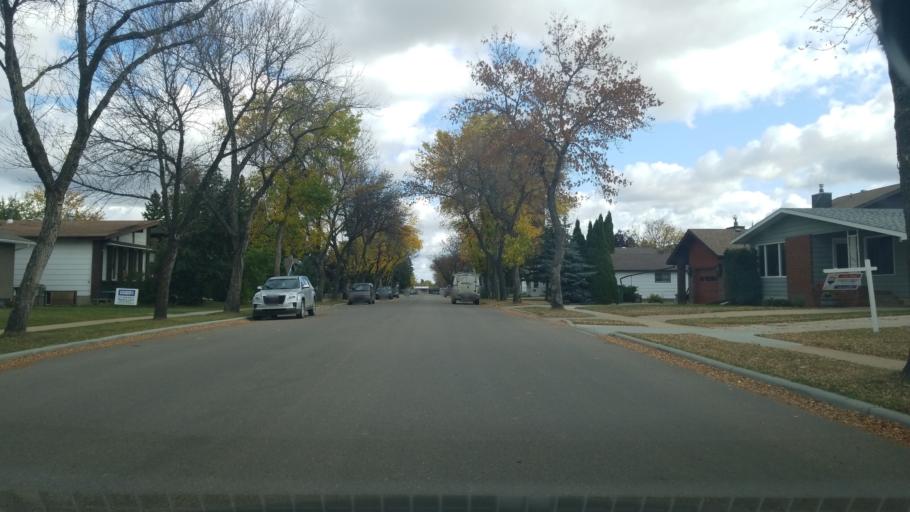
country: CA
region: Saskatchewan
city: Lloydminster
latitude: 53.2807
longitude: -110.0128
